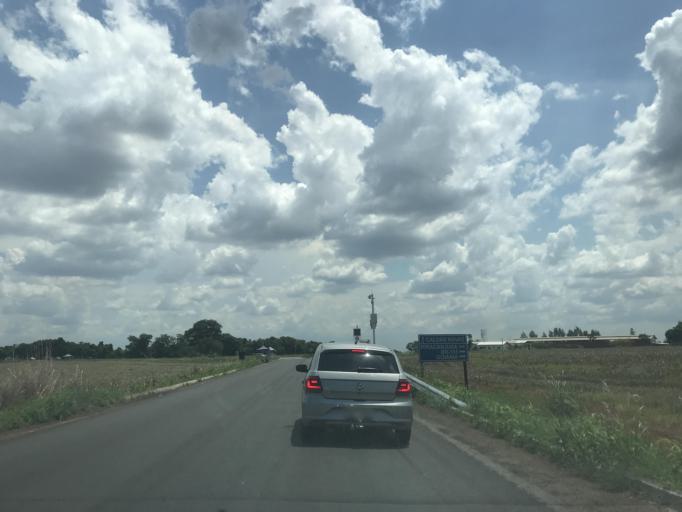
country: BR
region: Goias
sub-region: Piracanjuba
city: Piracanjuba
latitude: -17.3862
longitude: -48.8035
